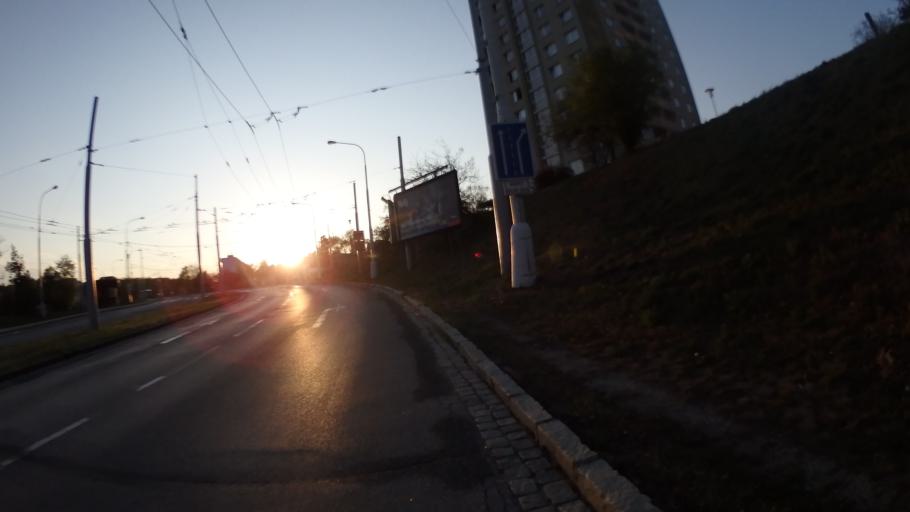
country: CZ
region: South Moravian
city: Troubsko
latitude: 49.1967
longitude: 16.5358
